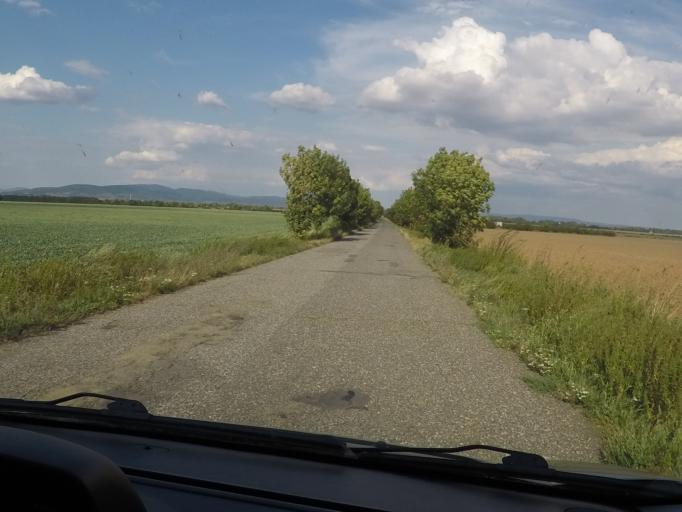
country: SK
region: Nitriansky
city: Tlmace
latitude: 48.2406
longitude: 18.4864
